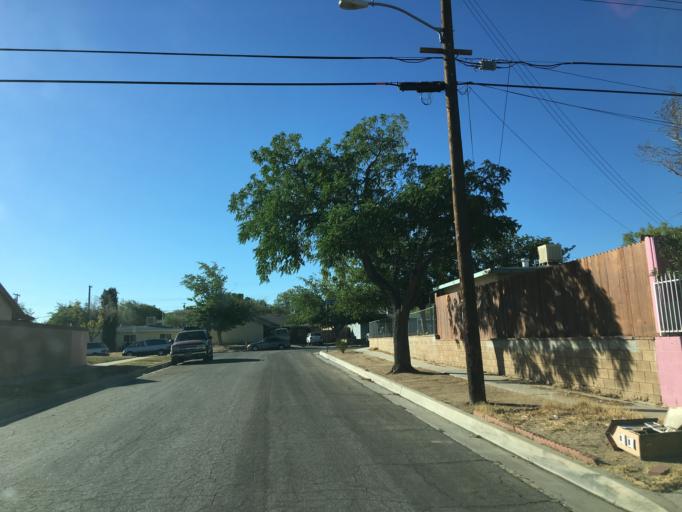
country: US
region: California
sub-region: Los Angeles County
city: Desert View Highlands
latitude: 34.5891
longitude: -118.1592
